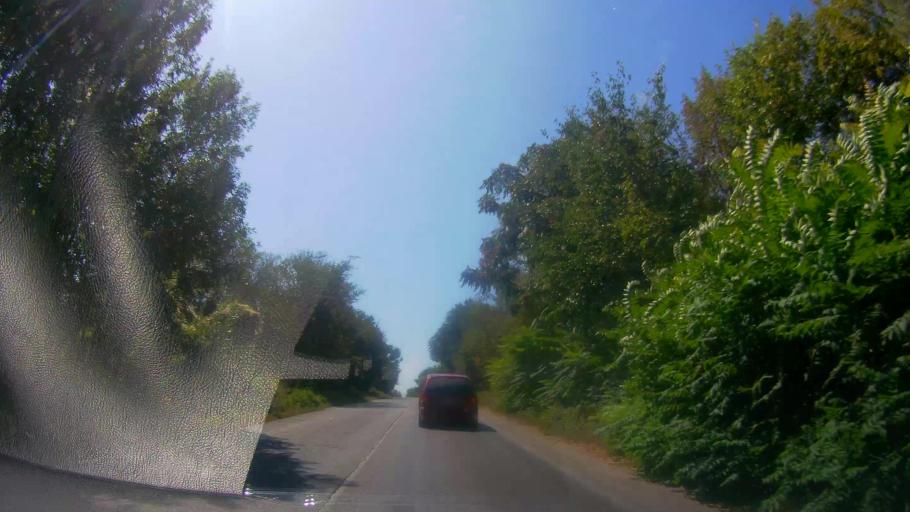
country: BG
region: Veliko Turnovo
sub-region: Obshtina Gorna Oryakhovitsa
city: Purvomaytsi
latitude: 43.2383
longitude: 25.6414
